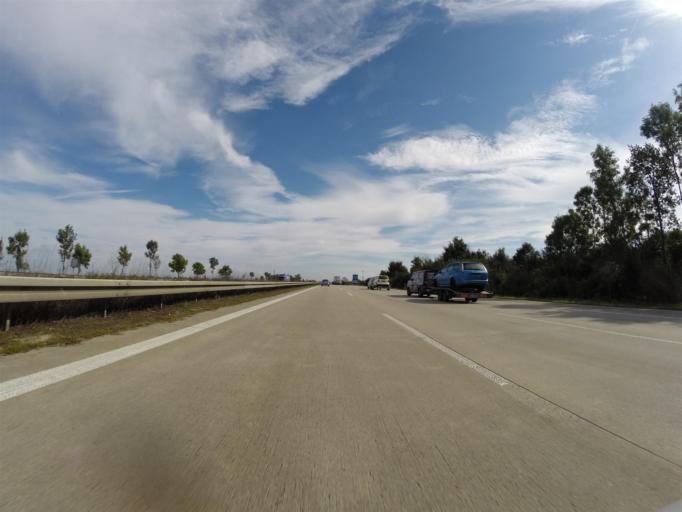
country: DE
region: Saxony
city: Wilsdruff
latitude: 51.0612
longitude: 13.5518
